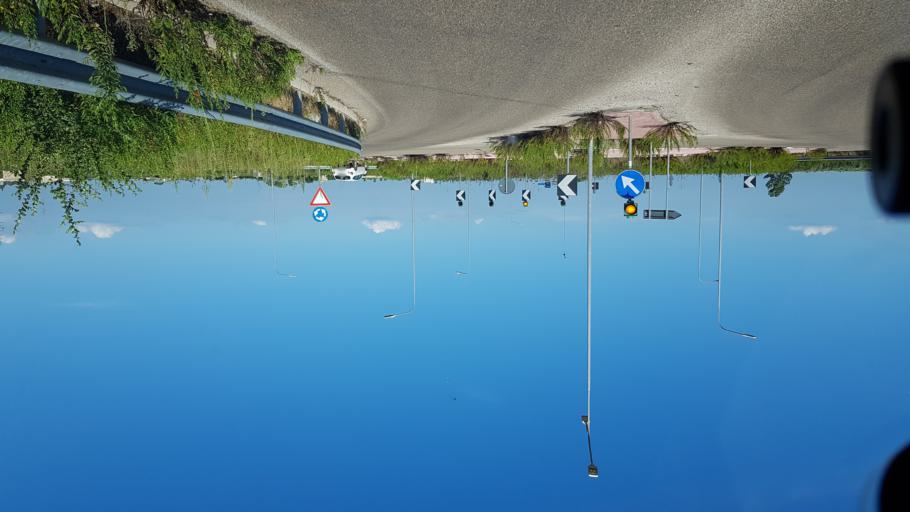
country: IT
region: Apulia
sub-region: Provincia di Lecce
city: Copertino
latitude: 40.2778
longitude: 18.0260
